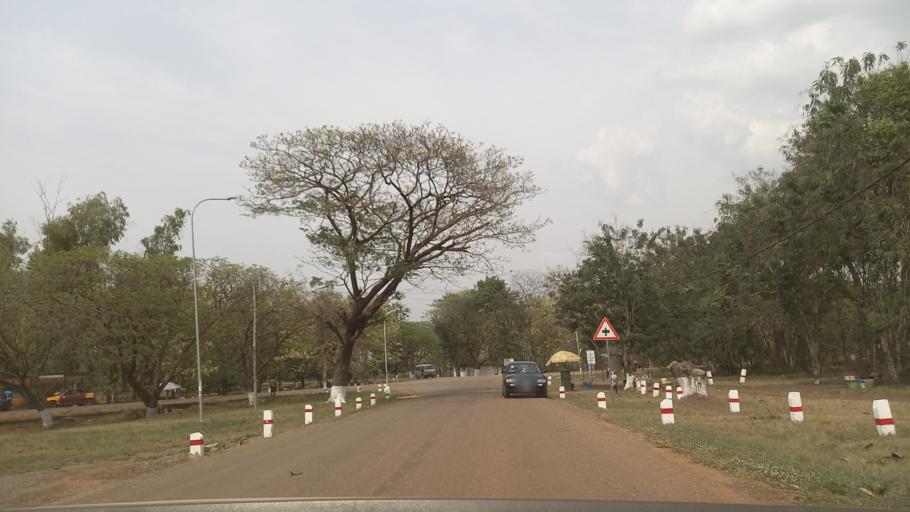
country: GH
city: Akropong
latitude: 6.0952
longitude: 0.1150
